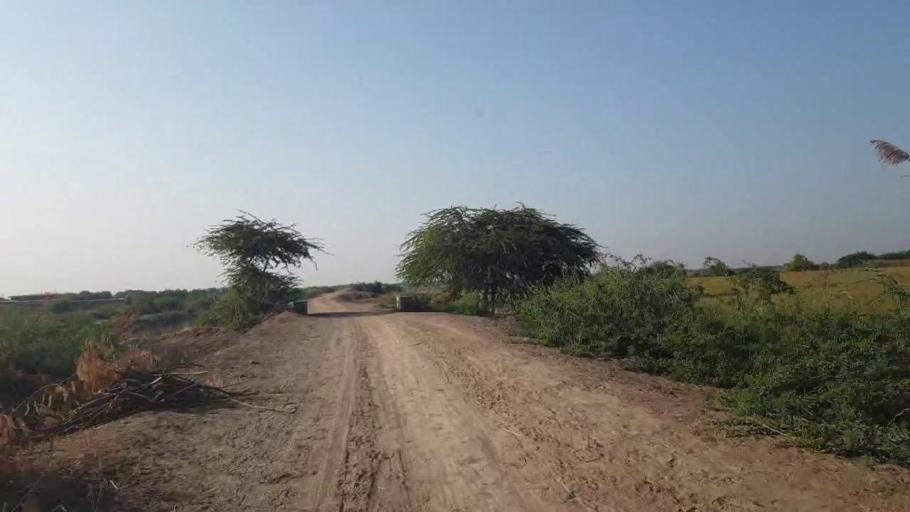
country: PK
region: Sindh
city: Badin
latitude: 24.4671
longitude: 68.7389
